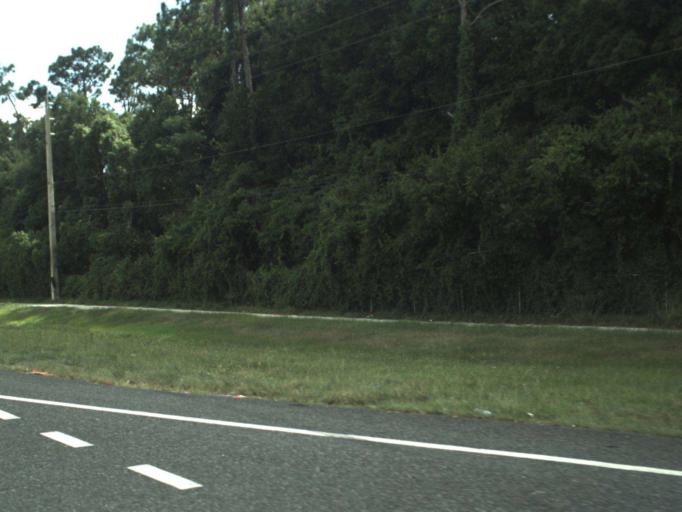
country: US
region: Florida
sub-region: Orange County
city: Fairview Shores
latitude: 28.5694
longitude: -81.4157
